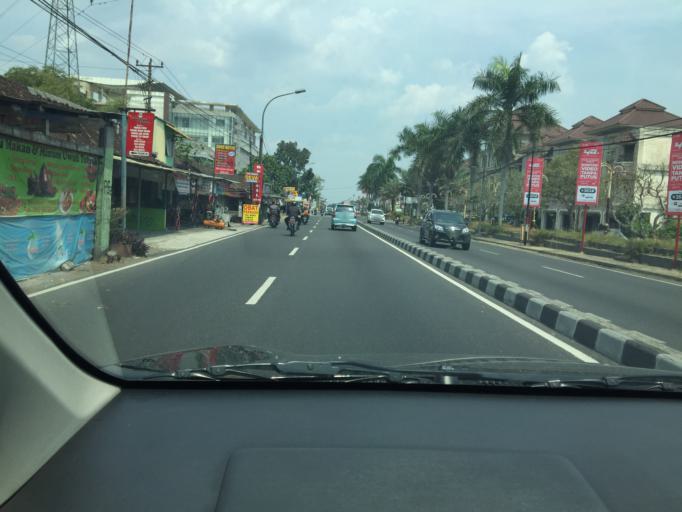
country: ID
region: Daerah Istimewa Yogyakarta
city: Sleman
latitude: -7.6854
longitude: 110.3408
